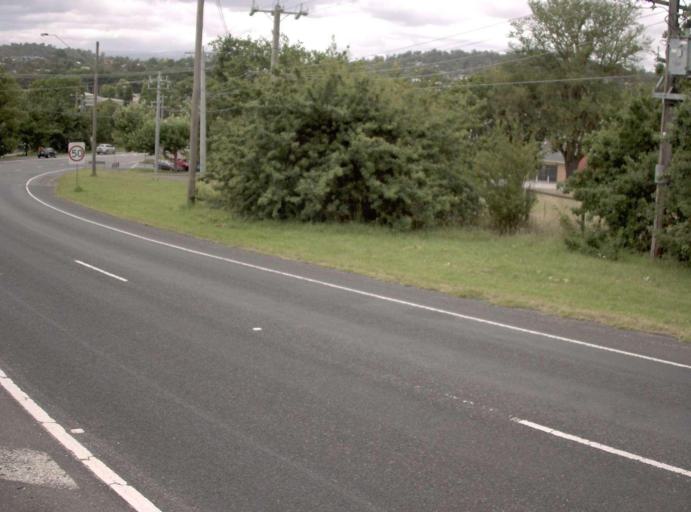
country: AU
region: Victoria
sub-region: Yarra Ranges
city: Lilydale
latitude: -37.7565
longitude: 145.3421
